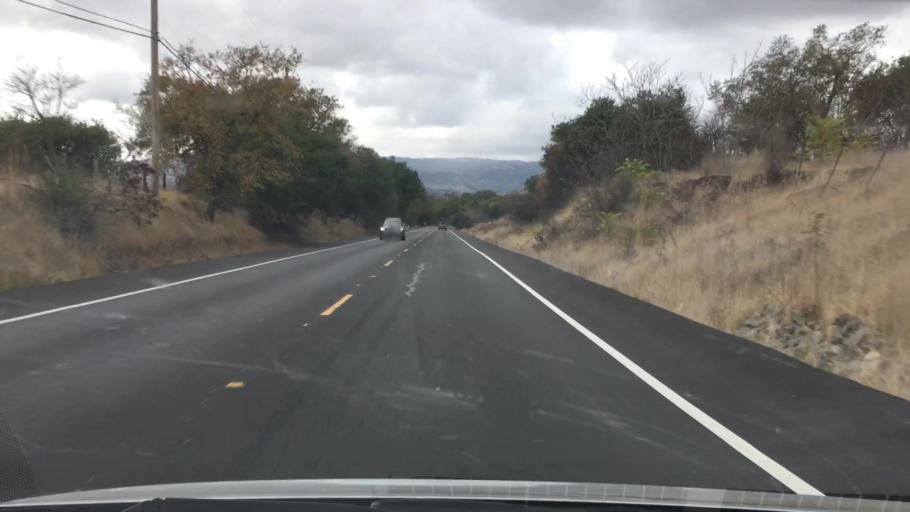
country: US
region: California
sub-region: Sonoma County
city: Sonoma
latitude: 38.2633
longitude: -122.4037
